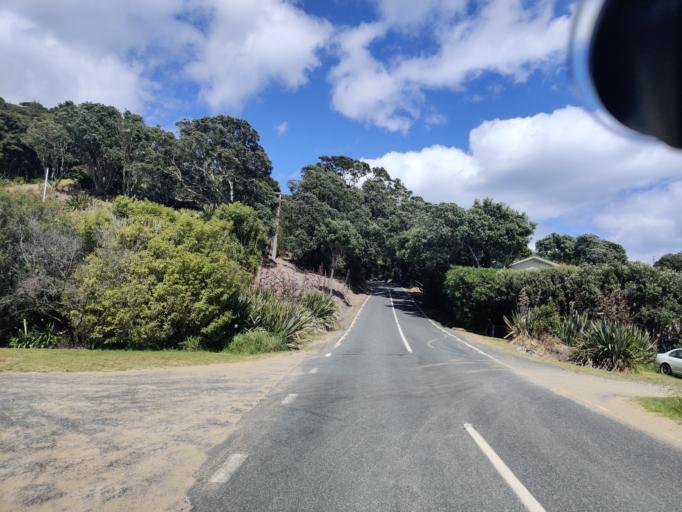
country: NZ
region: Northland
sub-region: Far North District
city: Paihia
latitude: -35.2577
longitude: 174.2427
